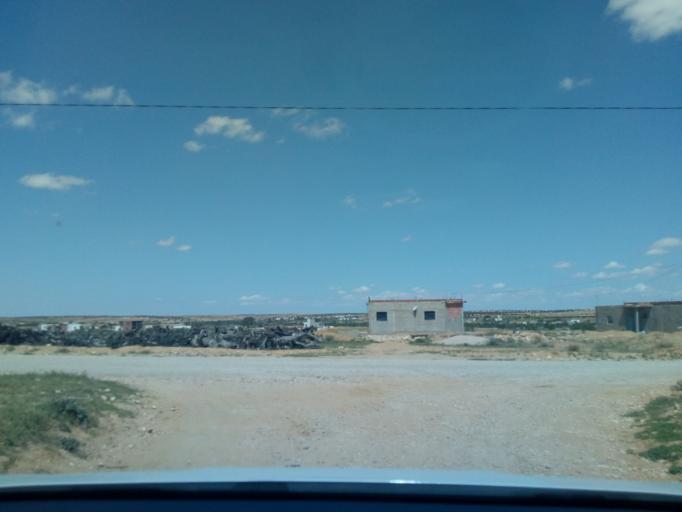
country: TN
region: Safaqis
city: Sfax
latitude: 34.7322
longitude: 10.4965
